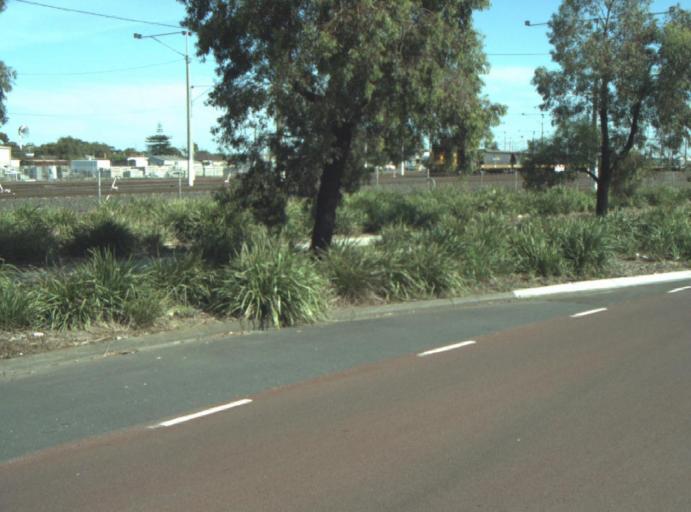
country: AU
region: Victoria
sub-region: Greater Geelong
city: Bell Park
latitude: -38.1200
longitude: 144.3533
